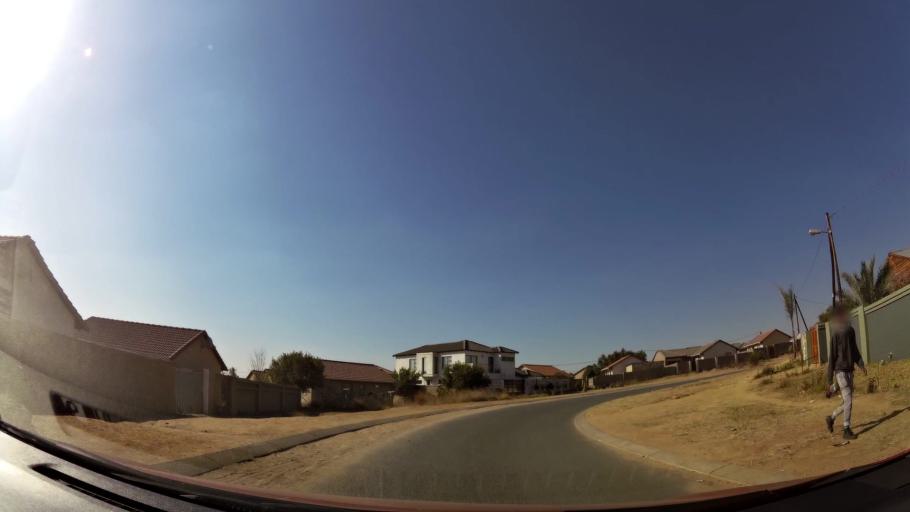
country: ZA
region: Gauteng
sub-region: West Rand District Municipality
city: Muldersdriseloop
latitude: -26.0365
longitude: 27.9256
